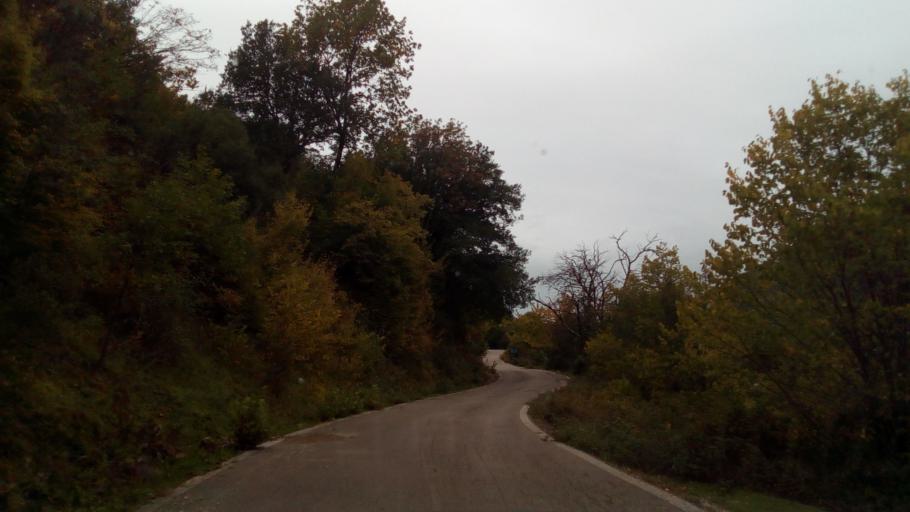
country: GR
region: West Greece
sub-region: Nomos Aitolias kai Akarnanias
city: Thermo
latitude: 38.5930
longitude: 21.8480
